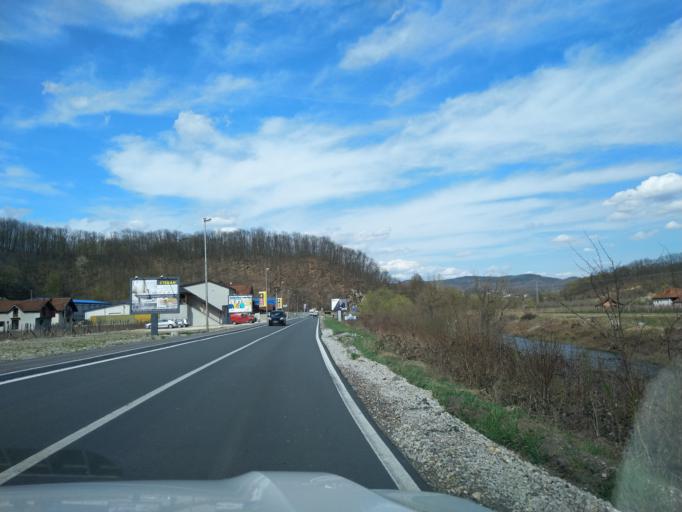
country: RS
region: Central Serbia
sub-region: Zlatiborski Okrug
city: Arilje
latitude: 43.7804
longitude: 20.1035
